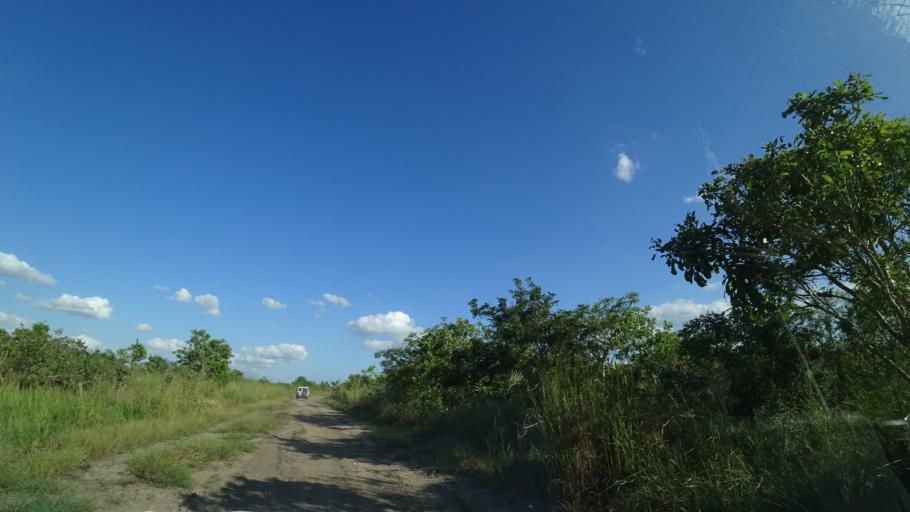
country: MZ
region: Sofala
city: Dondo
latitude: -19.3666
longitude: 34.5908
